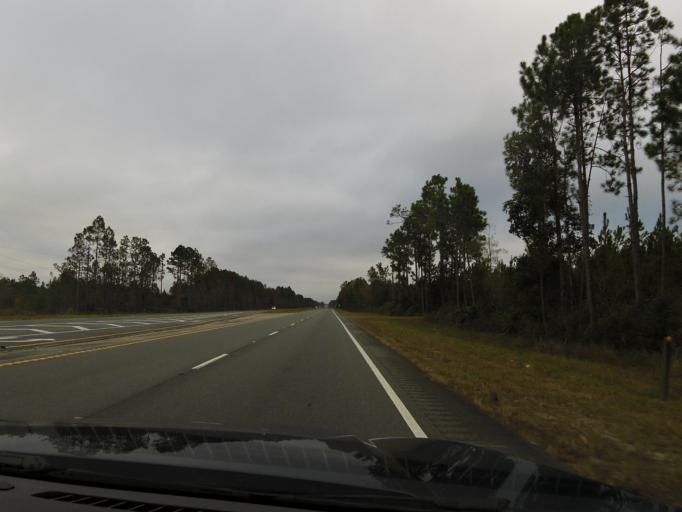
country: US
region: Georgia
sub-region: Charlton County
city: Folkston
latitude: 30.8848
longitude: -82.0410
